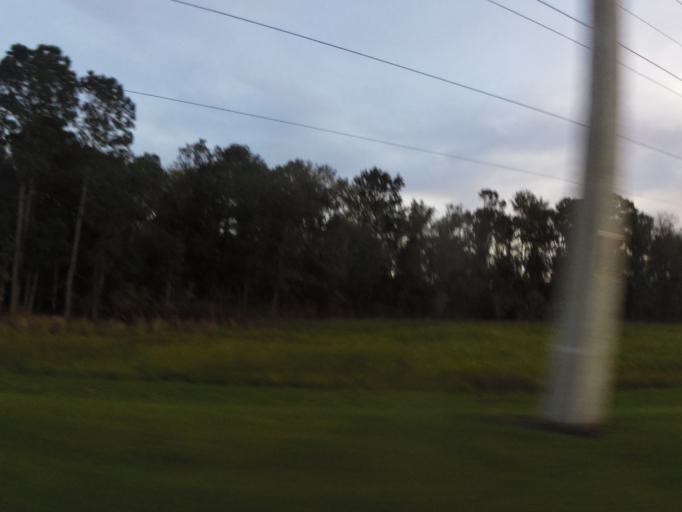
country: US
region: Florida
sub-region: Saint Johns County
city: Fruit Cove
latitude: 30.1529
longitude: -81.5227
